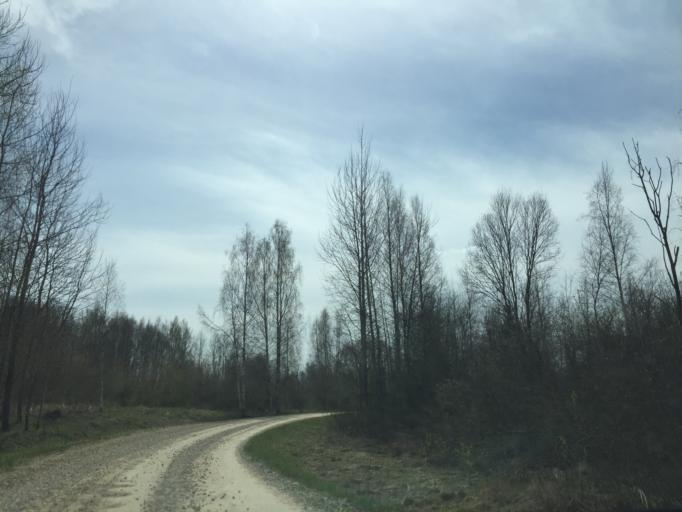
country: LV
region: Ludzas Rajons
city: Ludza
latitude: 56.5389
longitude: 27.5279
